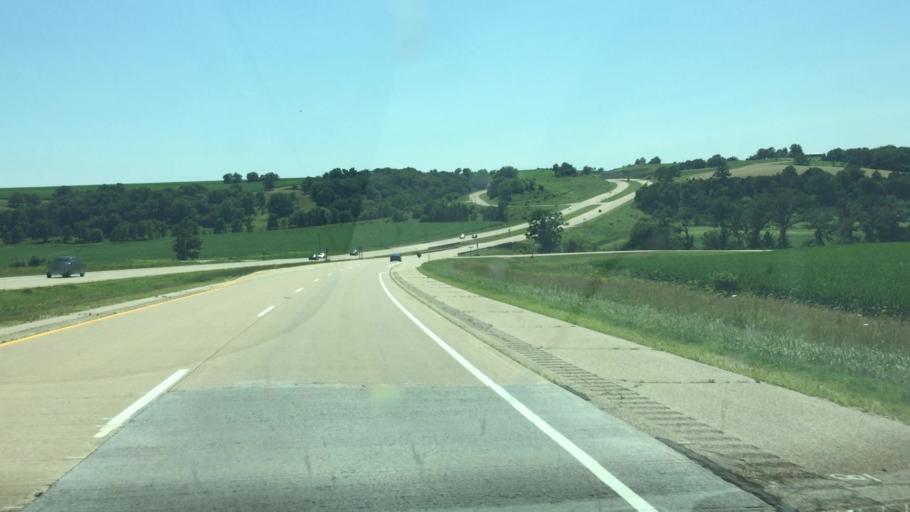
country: US
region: Wisconsin
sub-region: Iowa County
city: Mineral Point
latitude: 42.8267
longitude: -90.2372
